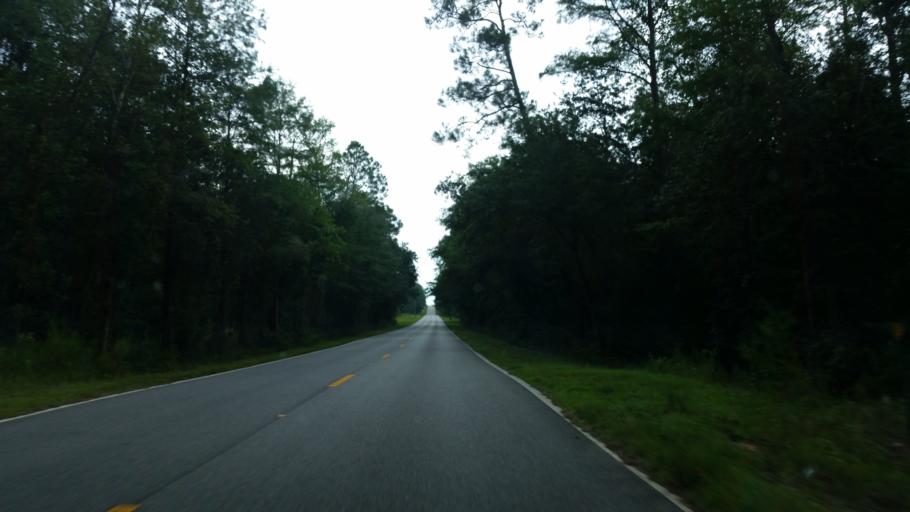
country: US
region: Florida
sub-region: Escambia County
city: Molino
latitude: 30.6813
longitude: -87.3872
